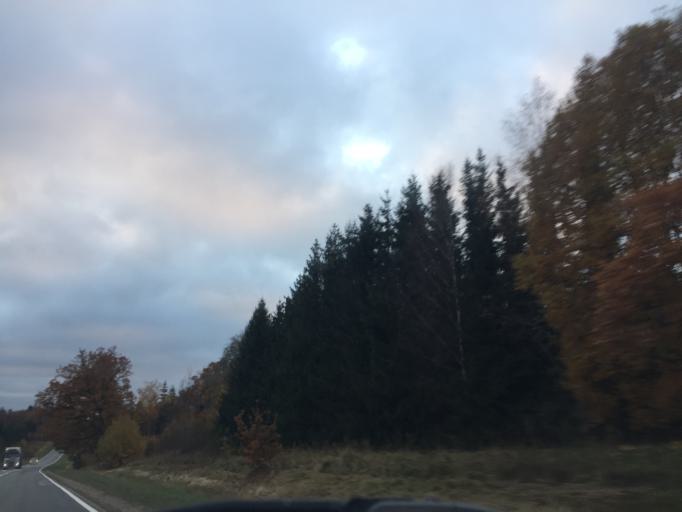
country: LV
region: Vainode
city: Vainode
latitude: 56.6082
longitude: 21.7693
